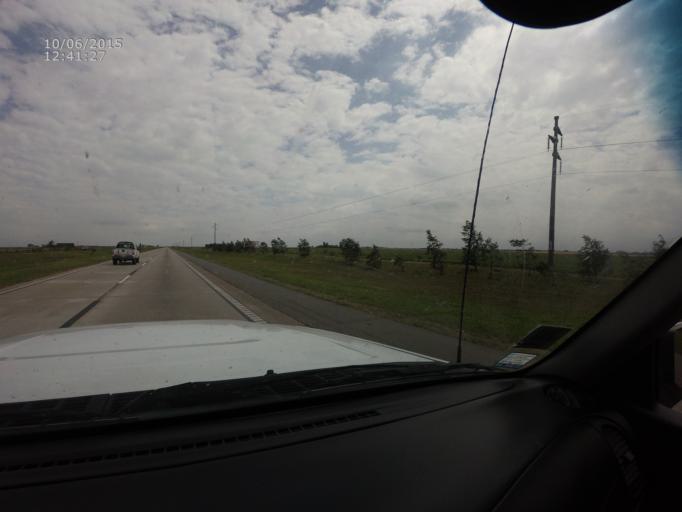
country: AR
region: Santa Fe
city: Canada de Gomez
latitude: -32.8611
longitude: -61.3052
